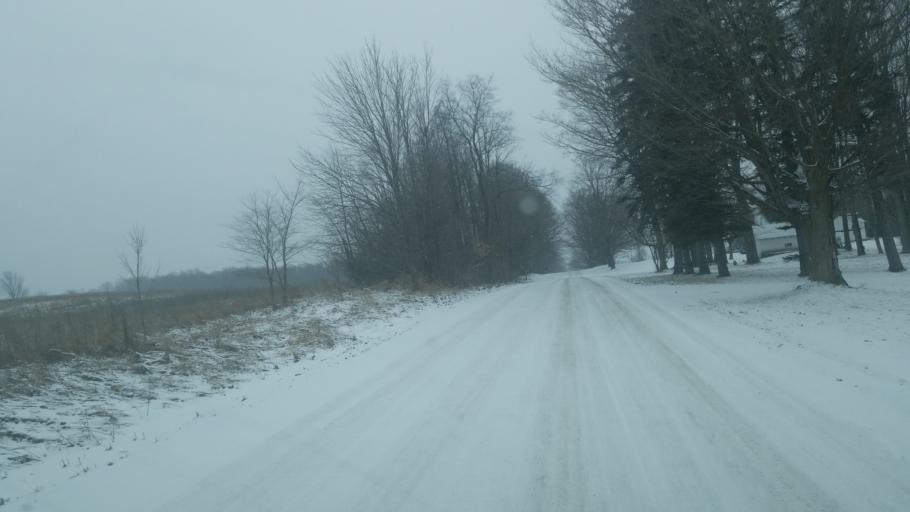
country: US
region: Michigan
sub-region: Osceola County
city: Reed City
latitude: 43.8400
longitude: -85.3940
